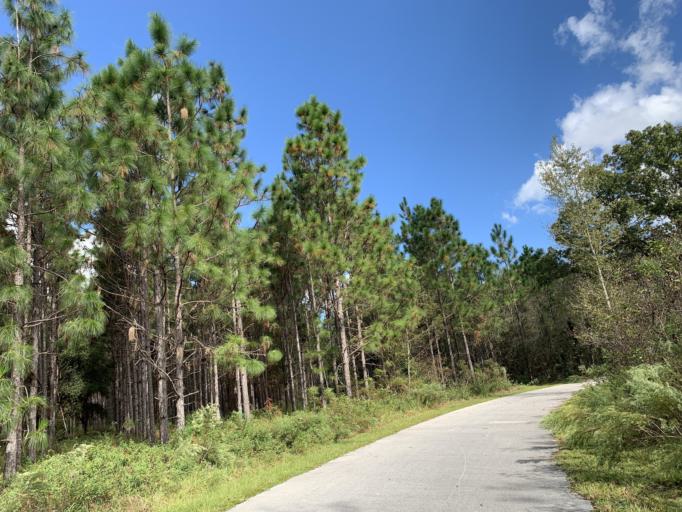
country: US
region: Florida
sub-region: Marion County
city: Silver Springs Shores
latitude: 29.1513
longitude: -82.0451
